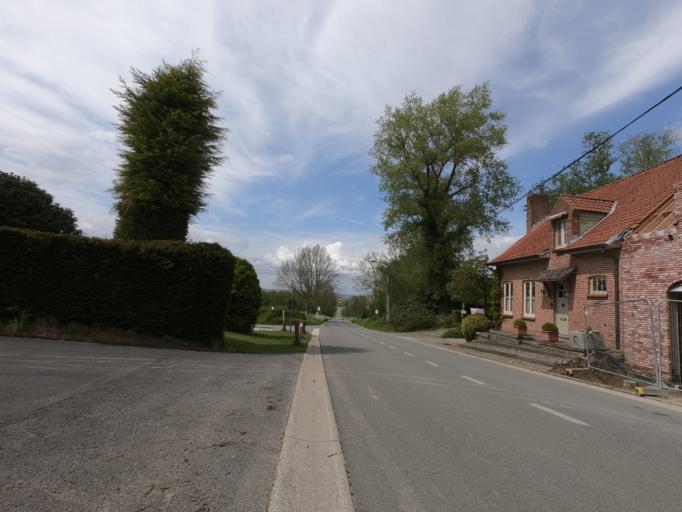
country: BE
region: Flanders
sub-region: Provincie Oost-Vlaanderen
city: Ronse
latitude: 50.7723
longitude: 3.5767
